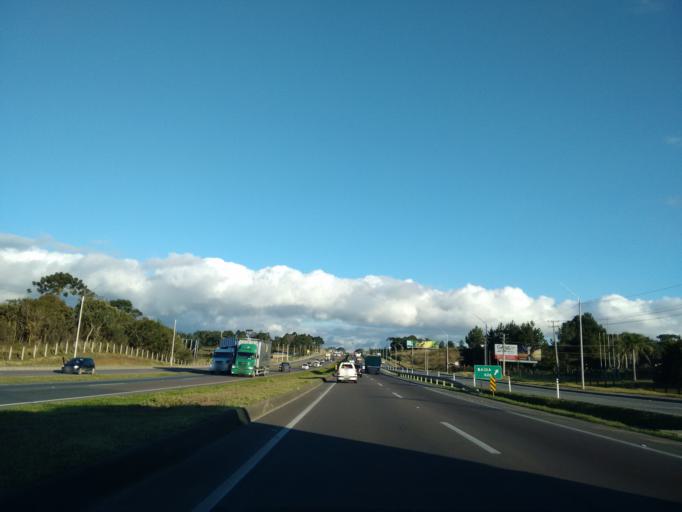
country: BR
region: Parana
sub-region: Sao Jose Dos Pinhais
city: Sao Jose dos Pinhais
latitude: -25.6695
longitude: -49.1523
